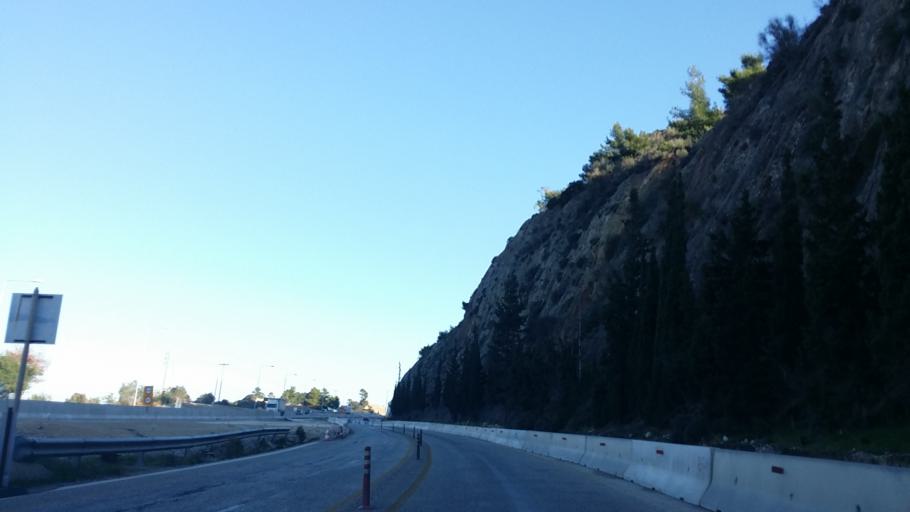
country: GR
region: West Greece
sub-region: Nomos Achaias
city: Akrata
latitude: 38.1742
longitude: 22.2468
